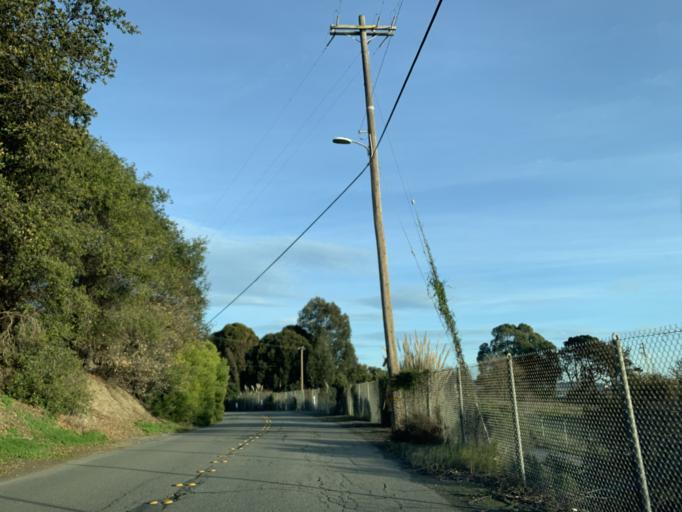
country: US
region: California
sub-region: Contra Costa County
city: North Richmond
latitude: 37.9336
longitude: -122.4063
